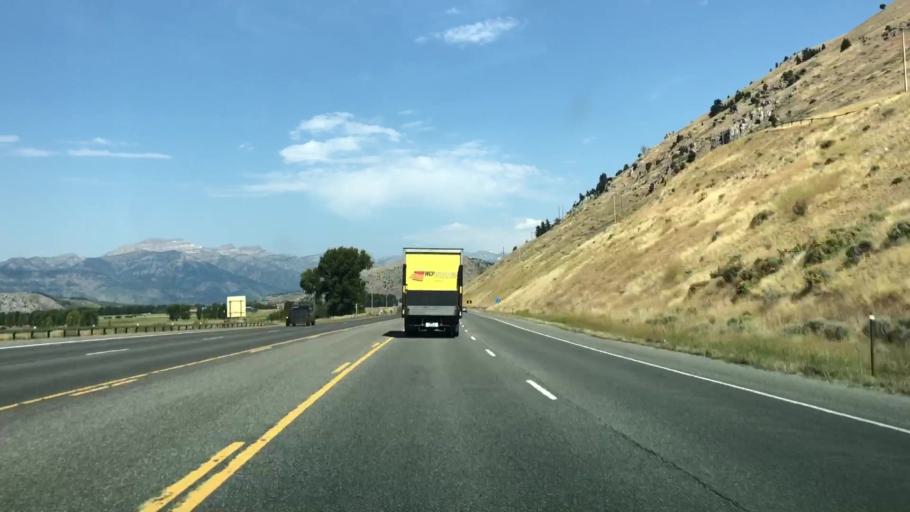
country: US
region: Wyoming
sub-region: Teton County
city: South Park
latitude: 43.4374
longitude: -110.7865
